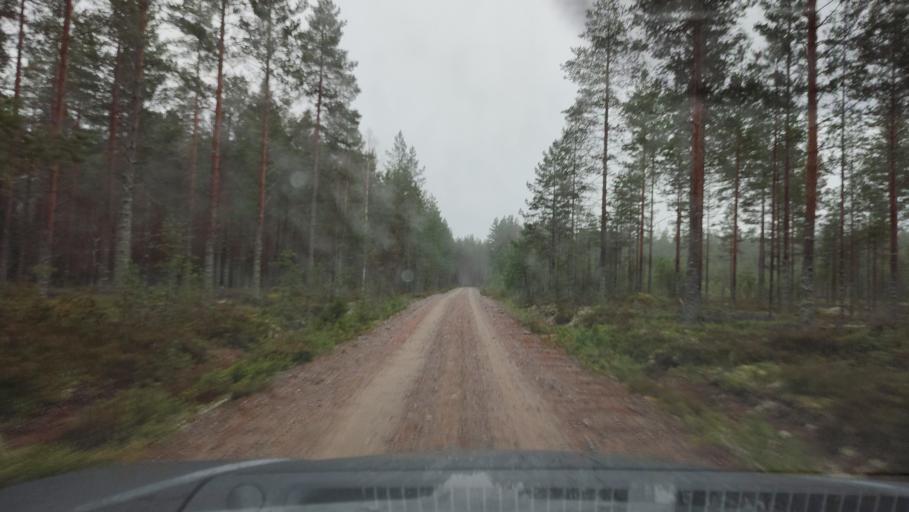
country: FI
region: Southern Ostrobothnia
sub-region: Suupohja
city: Karijoki
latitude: 62.1929
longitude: 21.7437
